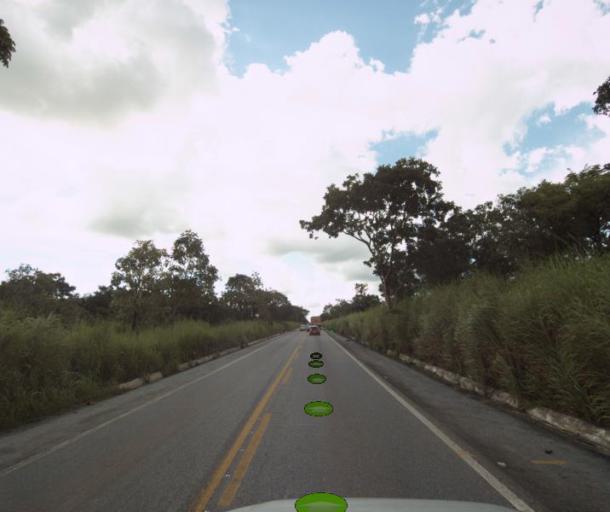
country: BR
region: Goias
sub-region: Porangatu
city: Porangatu
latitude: -13.2008
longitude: -49.1576
